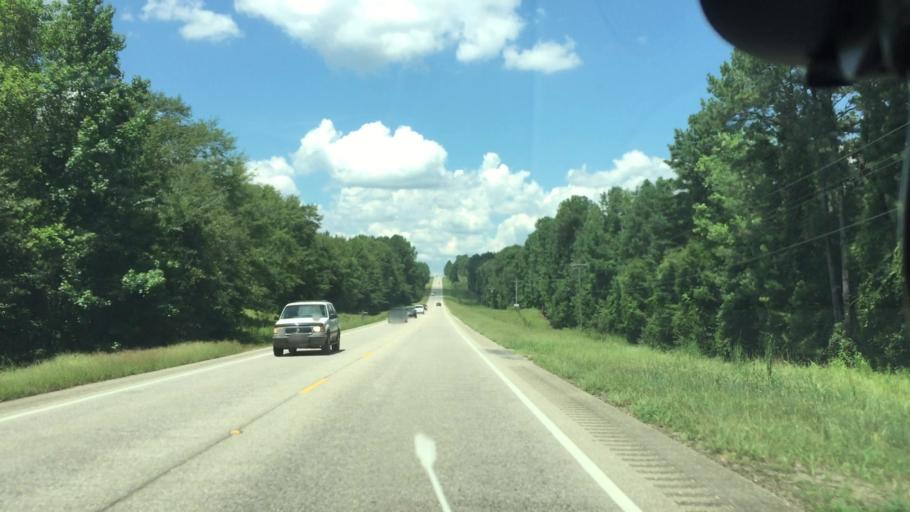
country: US
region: Alabama
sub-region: Pike County
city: Troy
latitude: 31.6639
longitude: -85.9534
